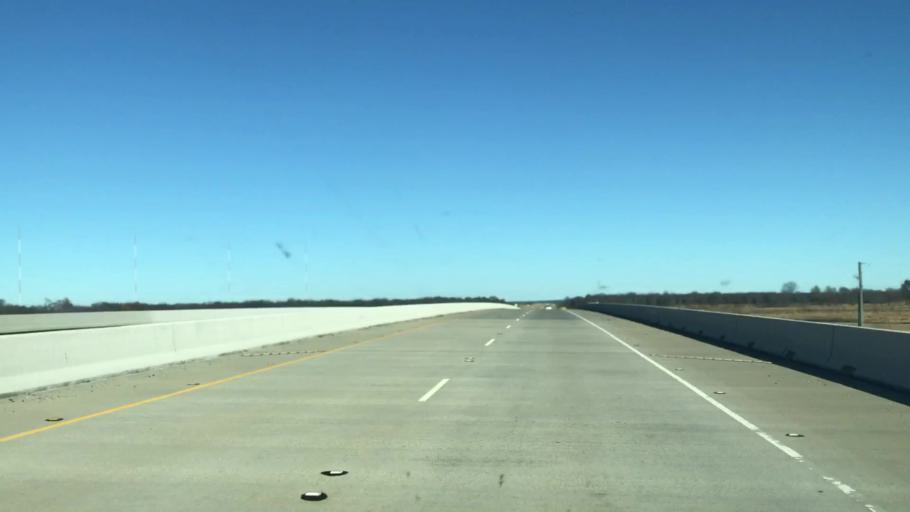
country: US
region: Louisiana
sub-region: Caddo Parish
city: Blanchard
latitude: 32.6742
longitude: -93.8497
